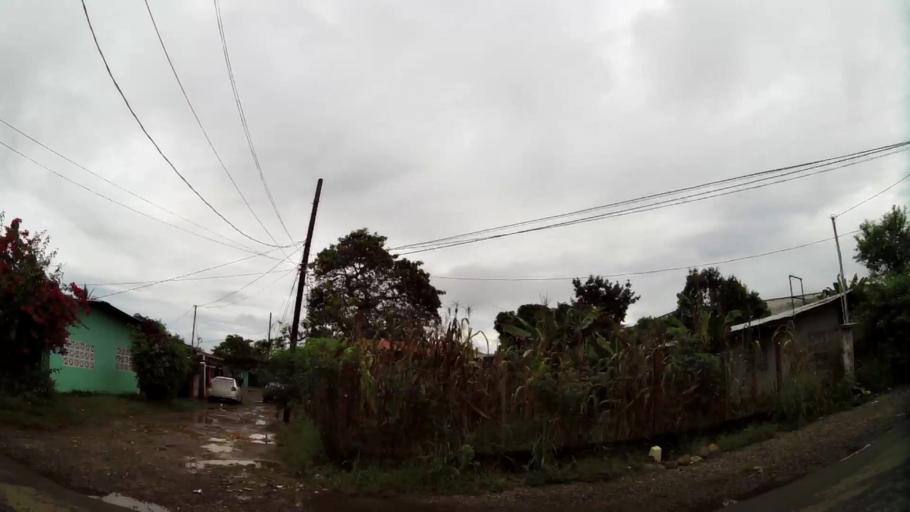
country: PA
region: Chiriqui
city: David
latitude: 8.4260
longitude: -82.4496
